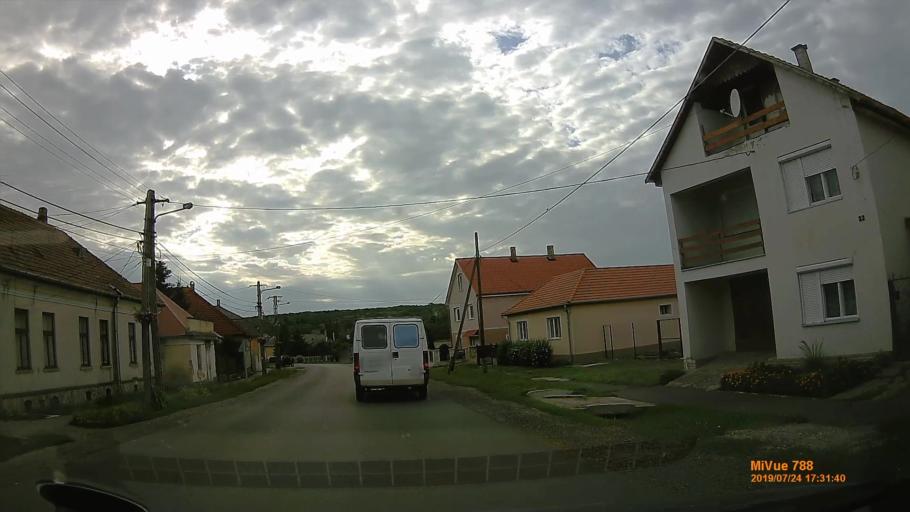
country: HU
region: Borsod-Abauj-Zemplen
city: Abaujszanto
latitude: 48.2840
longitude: 21.1863
